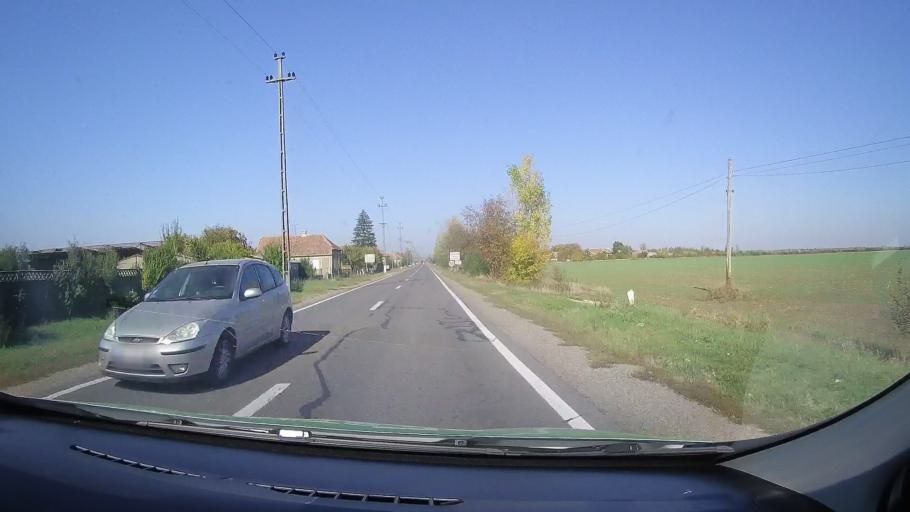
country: RO
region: Satu Mare
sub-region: Comuna Urziceni
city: Urziceni
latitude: 47.7251
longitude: 22.4113
